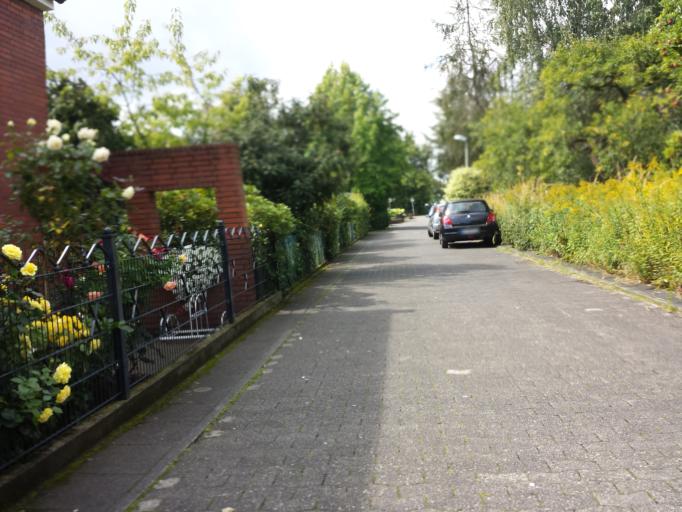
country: DE
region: North Rhine-Westphalia
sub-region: Regierungsbezirk Detmold
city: Guetersloh
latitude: 51.8910
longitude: 8.3747
